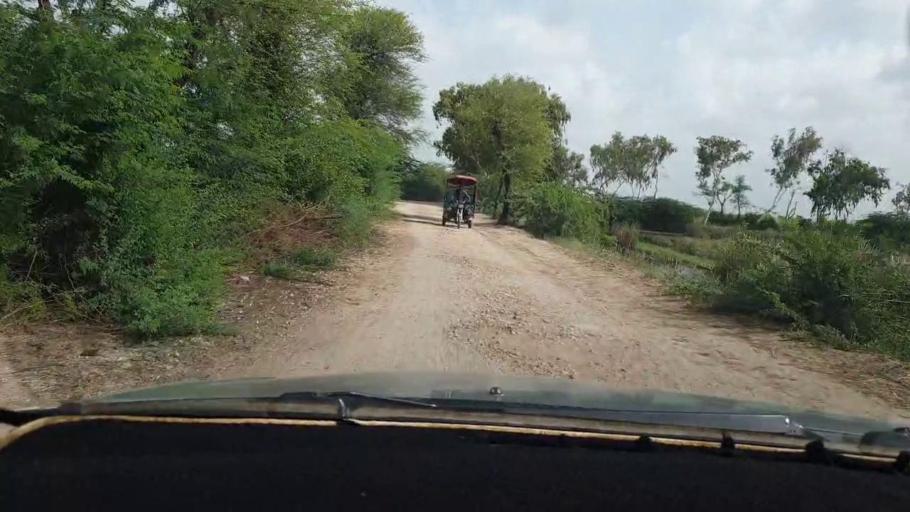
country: PK
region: Sindh
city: Tando Bago
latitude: 24.7719
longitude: 69.0244
